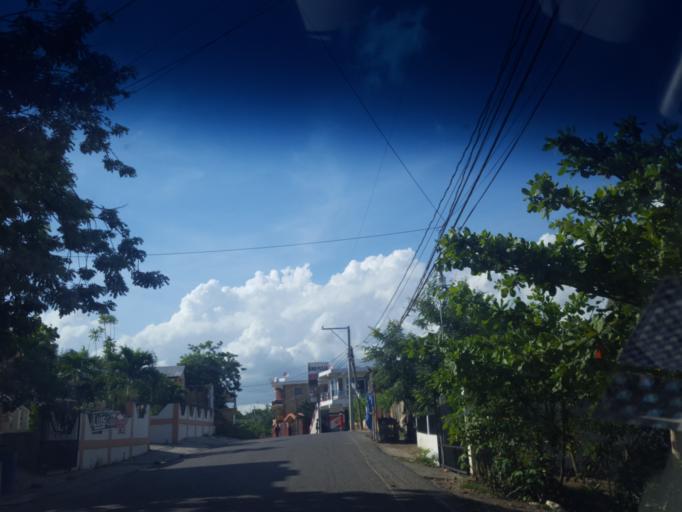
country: DO
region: La Vega
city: Rio Verde Arriba
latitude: 19.3587
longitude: -70.6052
